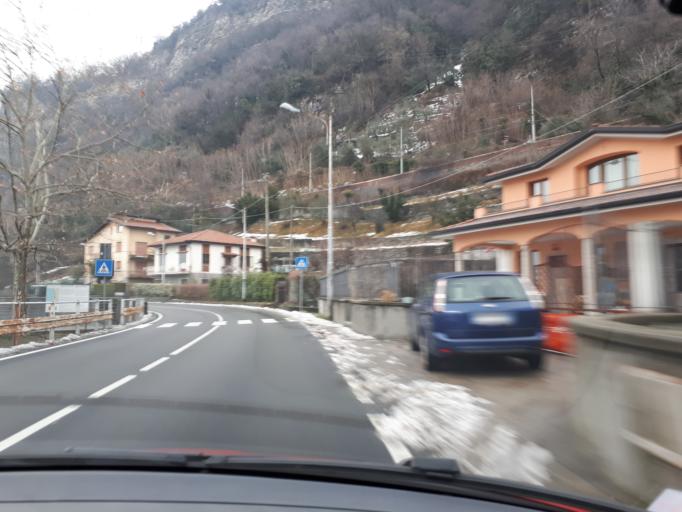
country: IT
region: Lombardy
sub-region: Provincia di Lecco
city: Mandello del Lario
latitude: 45.9398
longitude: 9.3126
